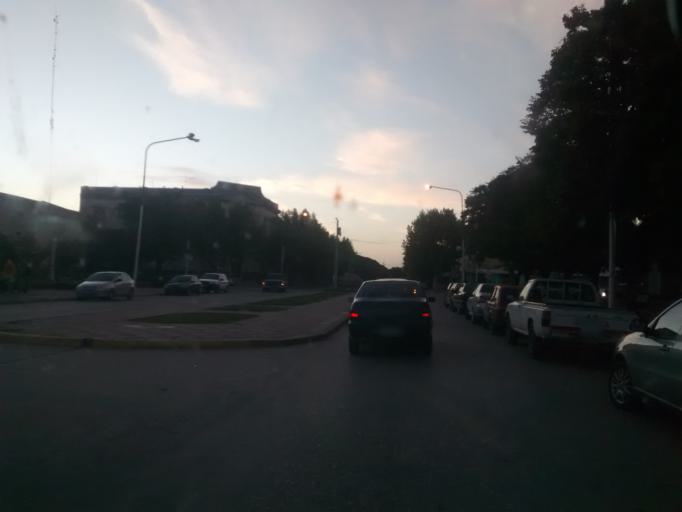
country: AR
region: Buenos Aires
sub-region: Partido de Loberia
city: Loberia
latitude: -38.1640
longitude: -58.7825
